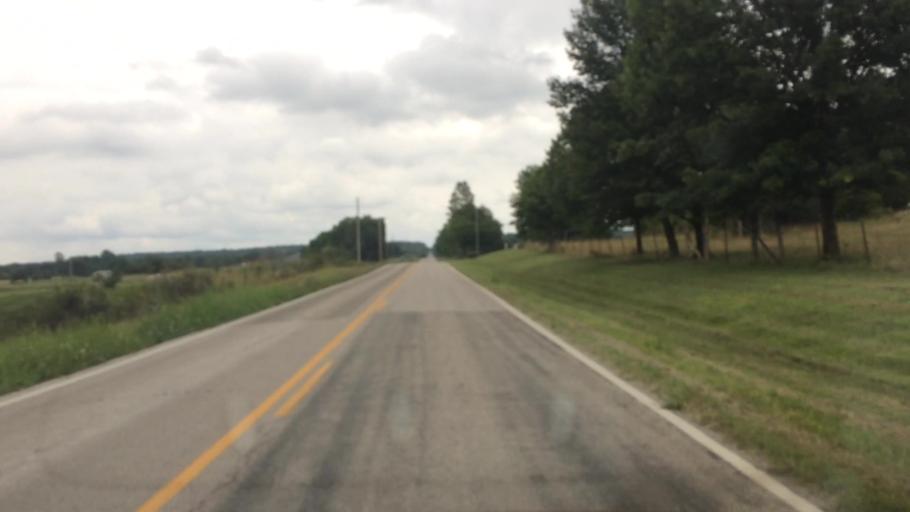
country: US
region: Missouri
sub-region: Webster County
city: Marshfield
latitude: 37.3413
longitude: -93.0010
